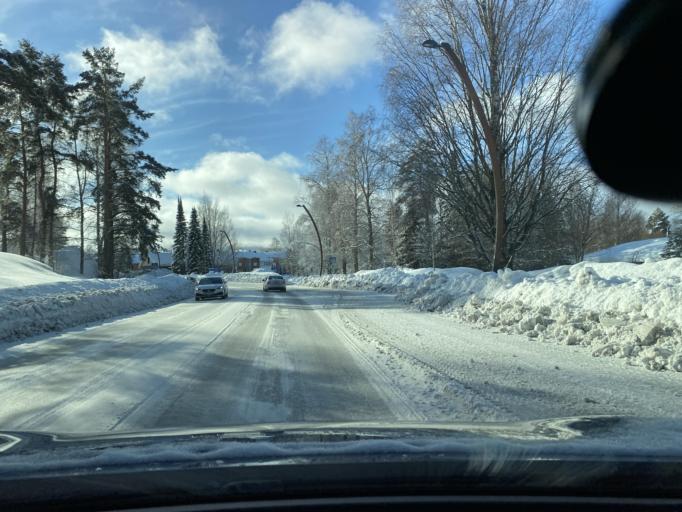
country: FI
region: Southern Savonia
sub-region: Mikkeli
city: Kangasniemi
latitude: 61.9918
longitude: 26.6441
